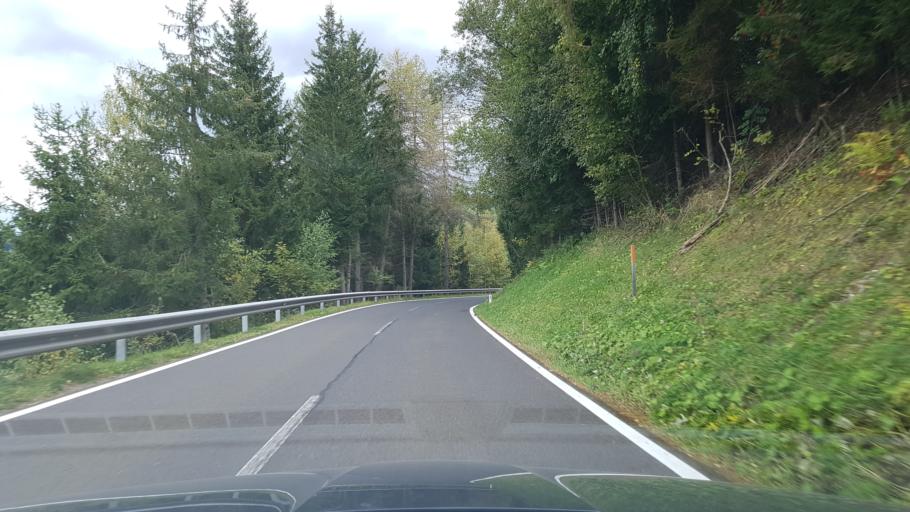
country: AT
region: Styria
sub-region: Politischer Bezirk Murtal
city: Kleinlobming
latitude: 47.1408
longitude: 14.8368
